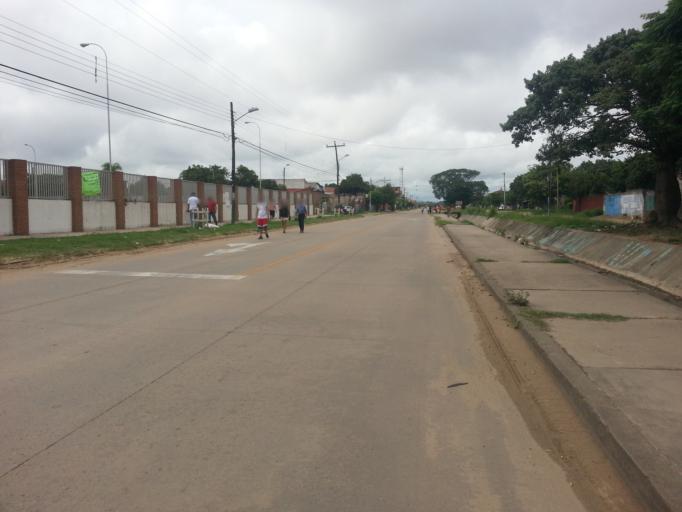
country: BO
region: Santa Cruz
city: Santa Cruz de la Sierra
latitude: -17.8182
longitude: -63.2062
